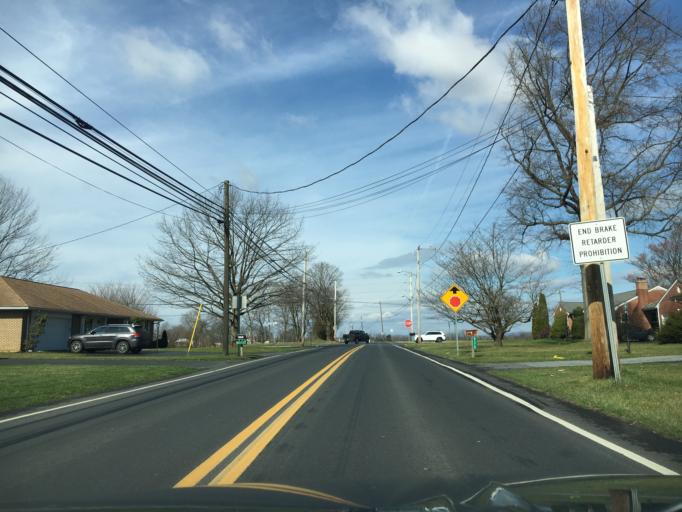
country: US
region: Pennsylvania
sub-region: Northampton County
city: Bath
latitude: 40.6824
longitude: -75.4086
